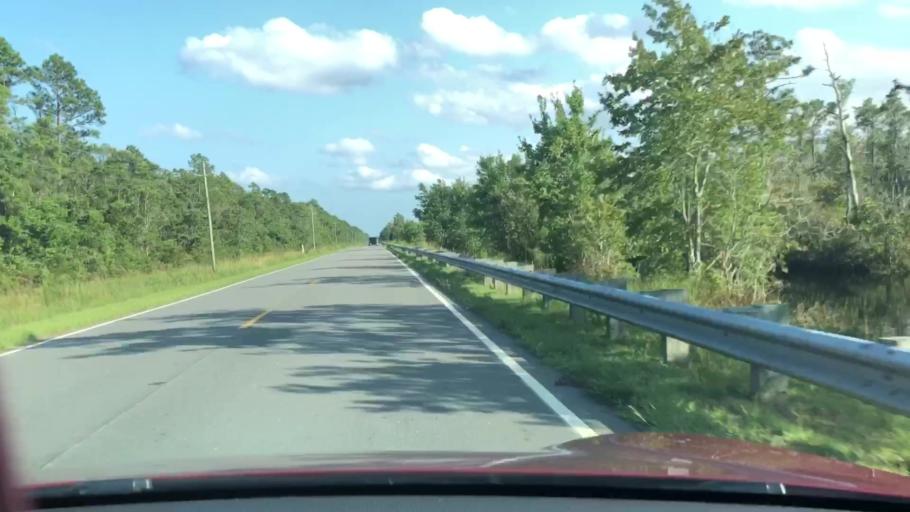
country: US
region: North Carolina
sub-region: Dare County
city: Manteo
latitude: 35.8091
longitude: -75.7896
